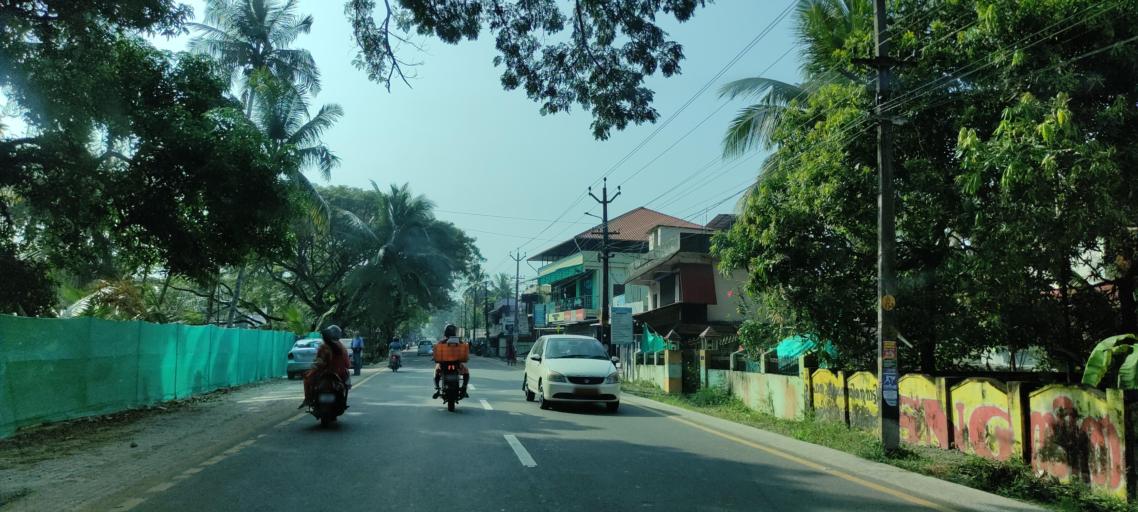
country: IN
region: Kerala
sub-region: Kottayam
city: Changanacheri
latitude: 9.3627
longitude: 76.4520
